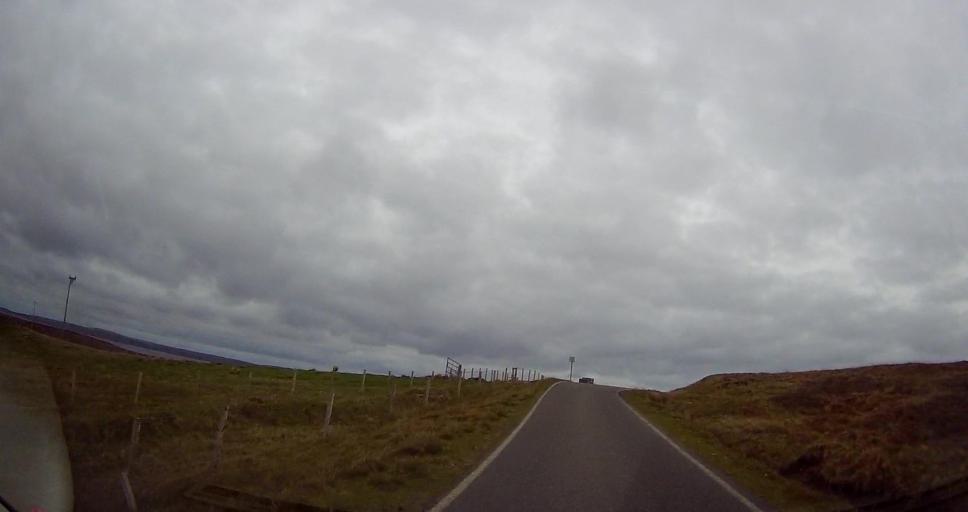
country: GB
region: Scotland
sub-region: Shetland Islands
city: Shetland
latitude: 60.5454
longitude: -1.0576
